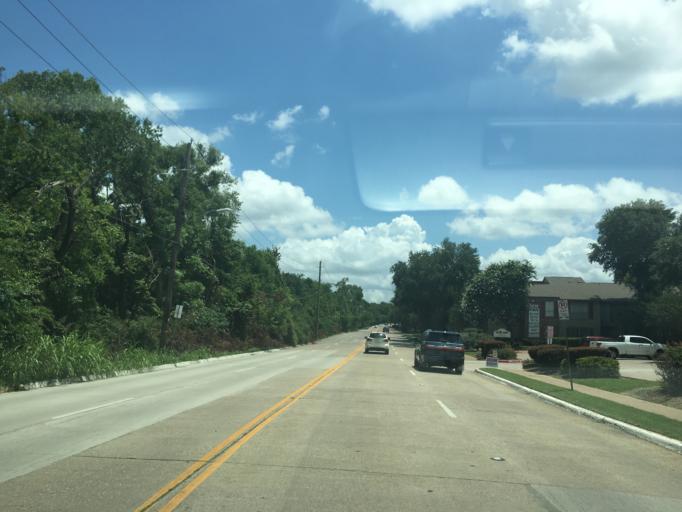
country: US
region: Texas
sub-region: Dallas County
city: University Park
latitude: 32.8742
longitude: -96.7533
